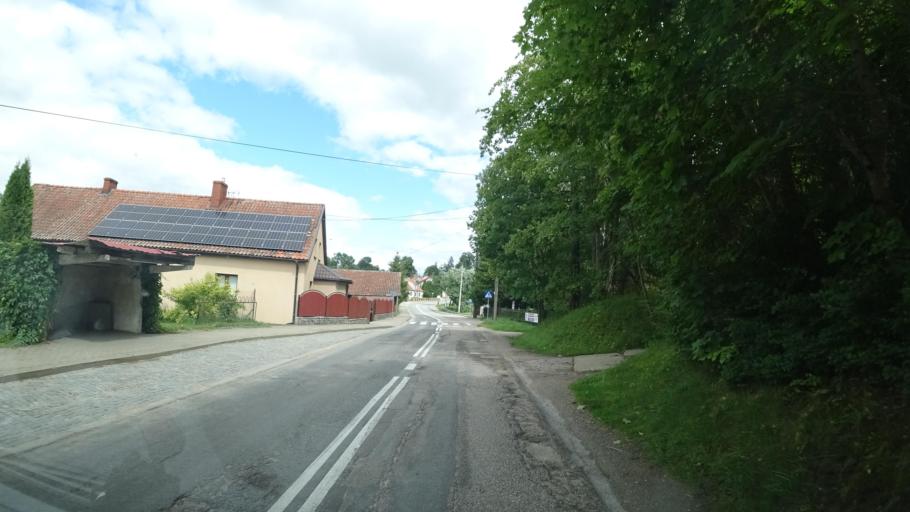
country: PL
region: Warmian-Masurian Voivodeship
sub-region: Powiat goldapski
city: Goldap
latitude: 54.2249
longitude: 22.2368
